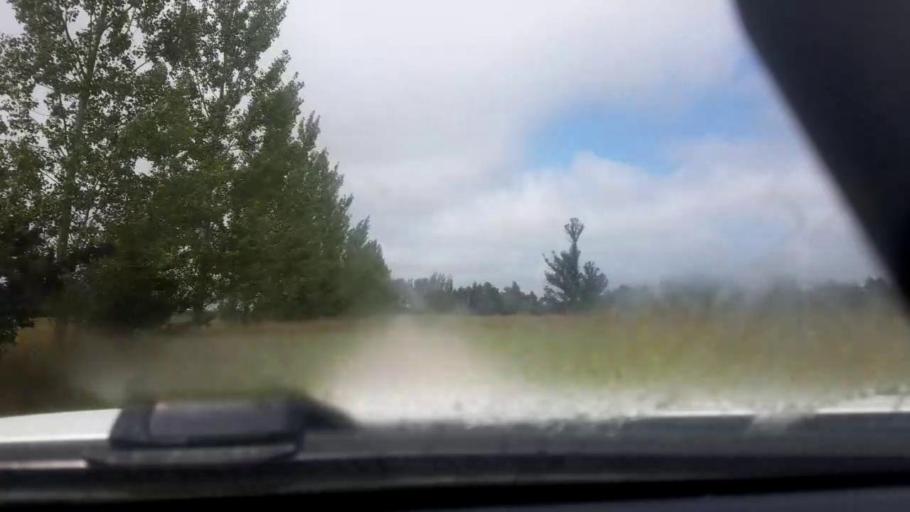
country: NZ
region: Canterbury
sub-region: Timaru District
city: Pleasant Point
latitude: -44.2000
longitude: 171.0904
